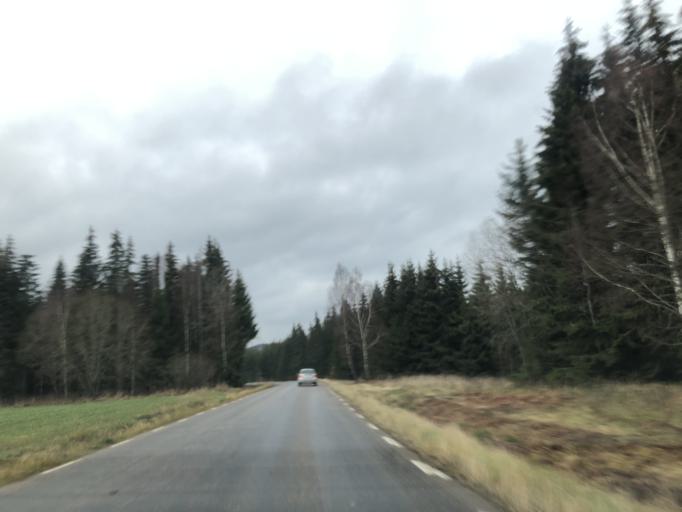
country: SE
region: Vaestra Goetaland
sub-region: Ulricehamns Kommun
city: Ulricehamn
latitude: 57.8987
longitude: 13.4894
